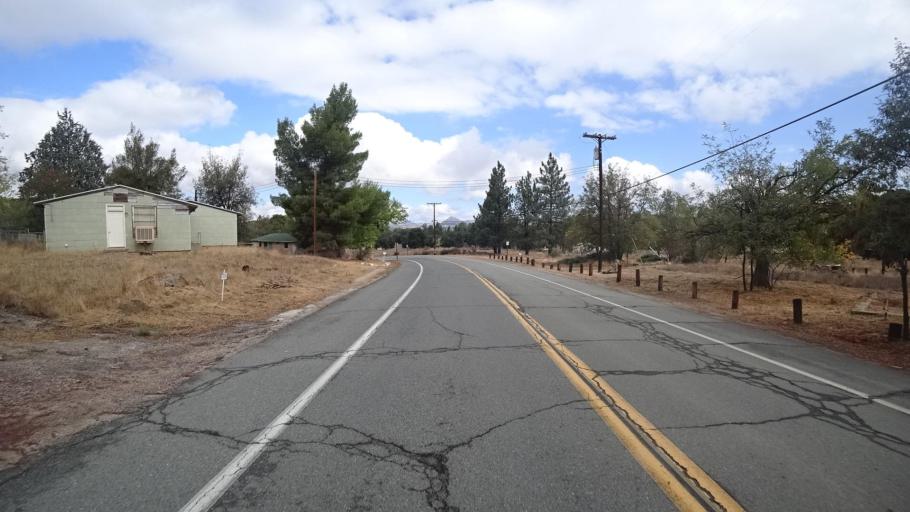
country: US
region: California
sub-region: San Diego County
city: Campo
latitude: 32.6034
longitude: -116.4703
